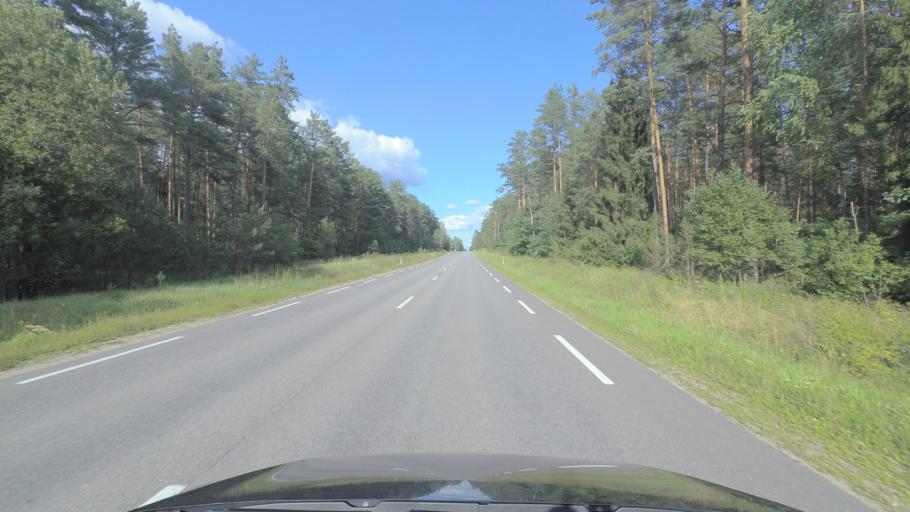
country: LT
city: Pabrade
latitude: 54.9550
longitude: 25.6765
